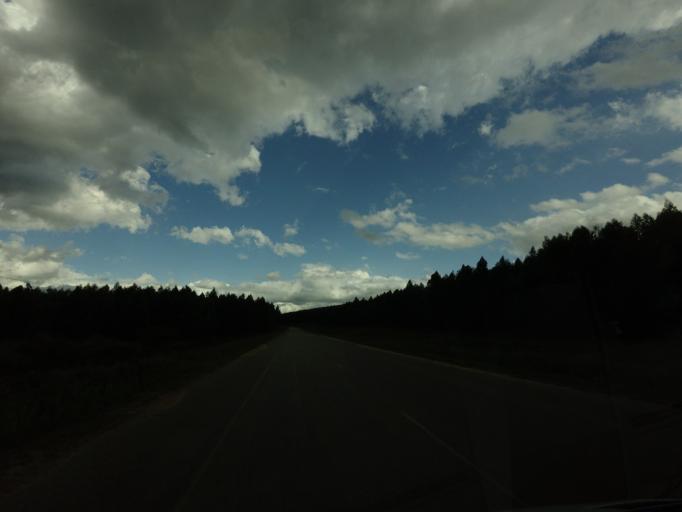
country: ZA
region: Mpumalanga
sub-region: Ehlanzeni District
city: Graksop
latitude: -24.9613
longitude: 30.9140
